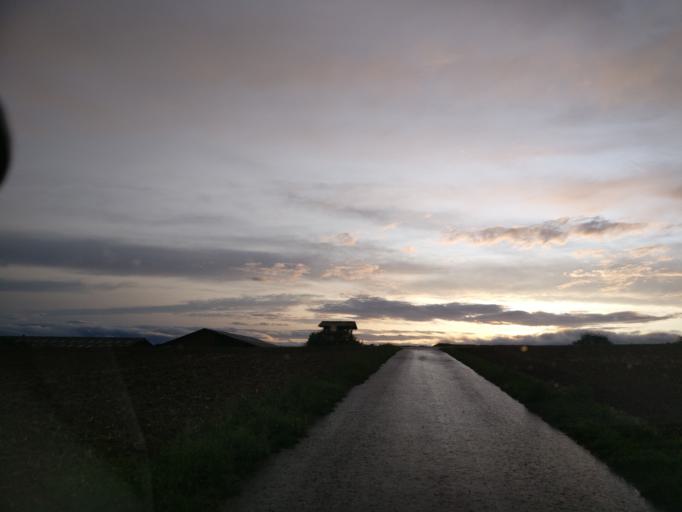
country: DE
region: Baden-Wuerttemberg
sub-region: Karlsruhe Region
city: Konigsbach-Stein
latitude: 48.9814
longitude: 8.5979
